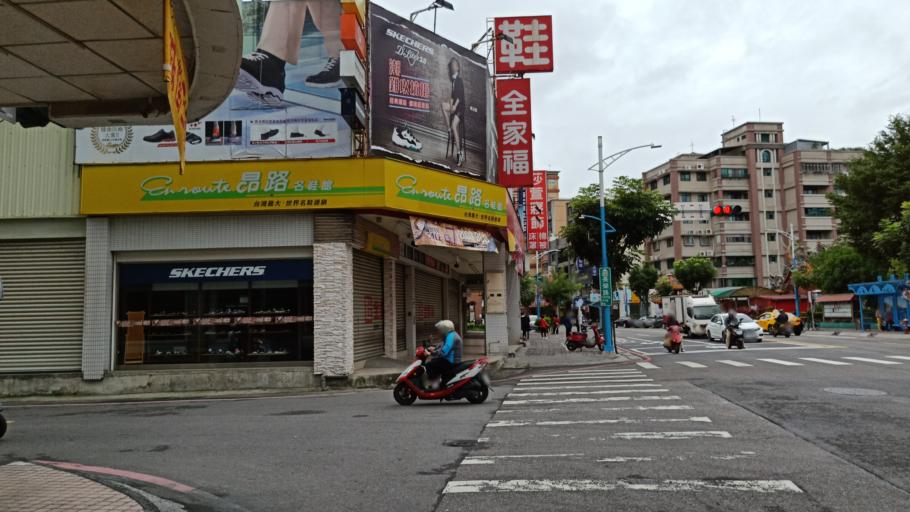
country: TW
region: Taipei
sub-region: Taipei
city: Banqiao
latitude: 25.0905
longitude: 121.4598
